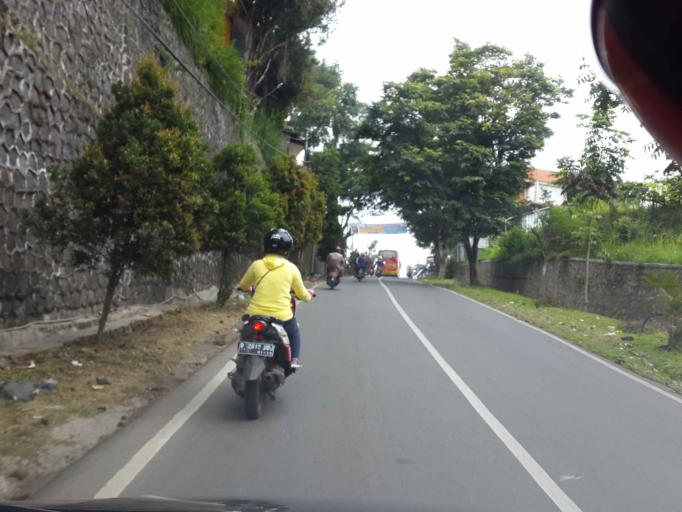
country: ID
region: West Java
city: Lembang
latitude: -6.8116
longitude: 107.5995
